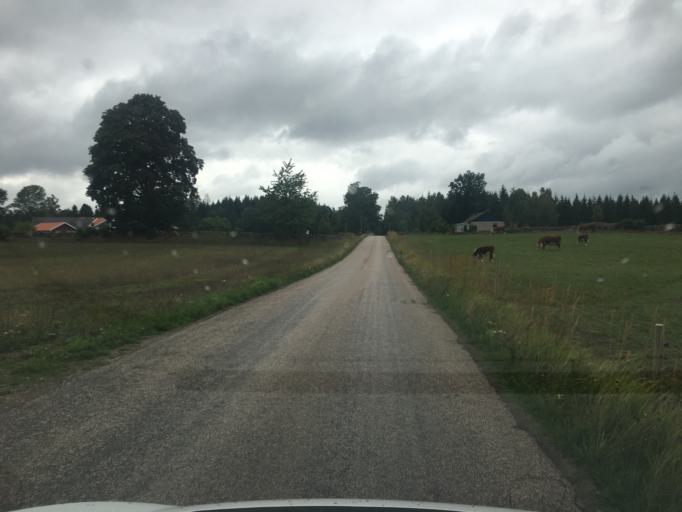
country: SE
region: Kronoberg
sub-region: Ljungby Kommun
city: Lagan
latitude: 56.9796
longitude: 14.0352
